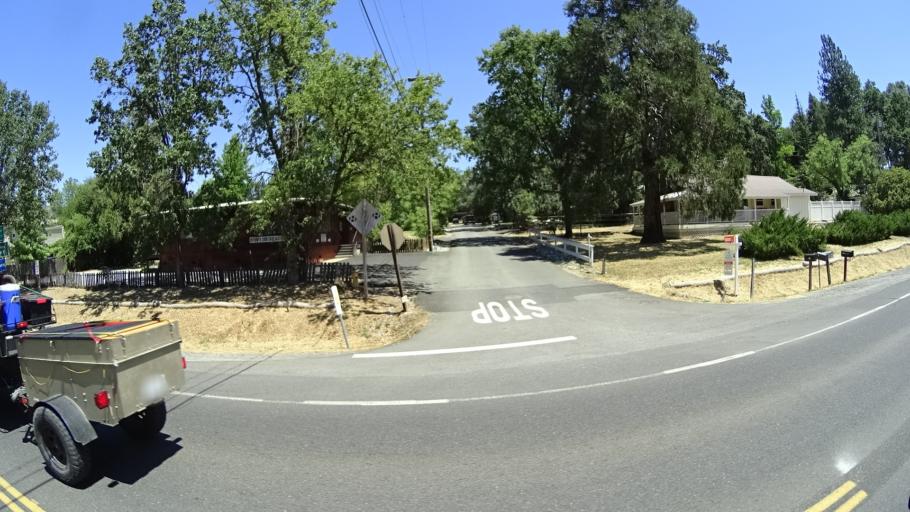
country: US
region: California
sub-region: Calaveras County
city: Murphys
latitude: 38.1356
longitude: -120.4562
